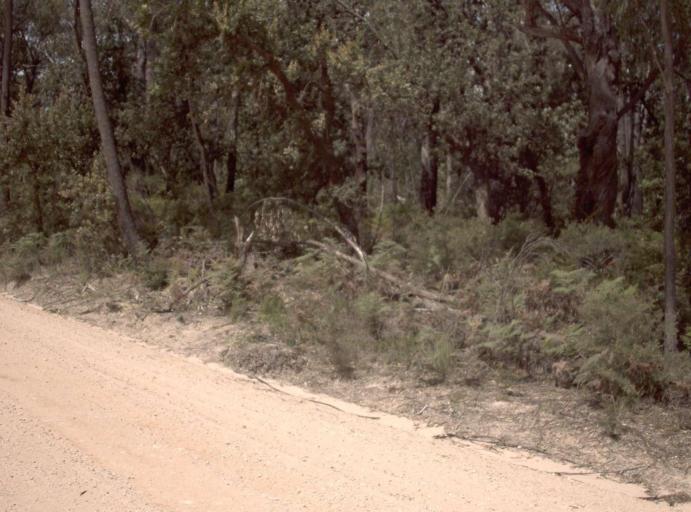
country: AU
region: Victoria
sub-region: East Gippsland
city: Lakes Entrance
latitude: -37.6587
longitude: 148.6386
